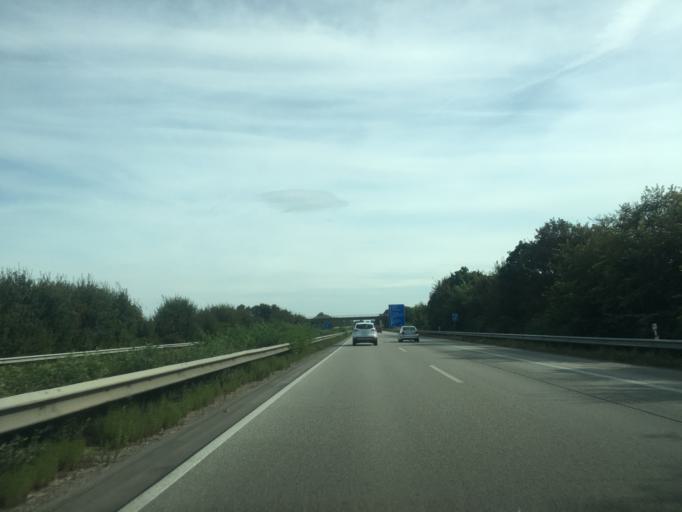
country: DE
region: Rheinland-Pfalz
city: Grossniedesheim
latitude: 49.5654
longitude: 8.3049
